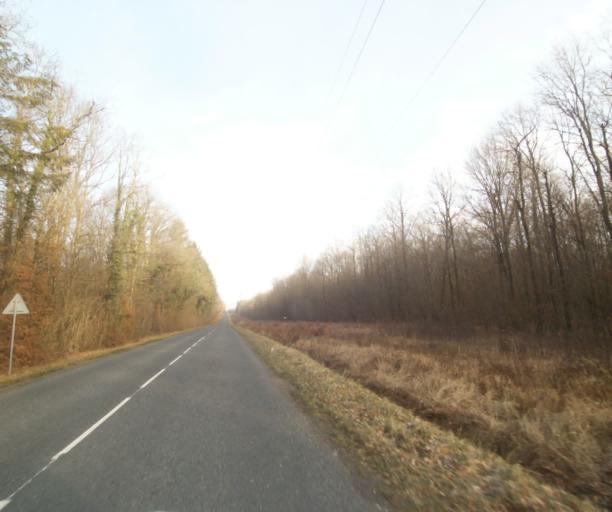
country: FR
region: Champagne-Ardenne
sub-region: Departement de la Haute-Marne
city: Bettancourt-la-Ferree
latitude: 48.6637
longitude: 4.9445
